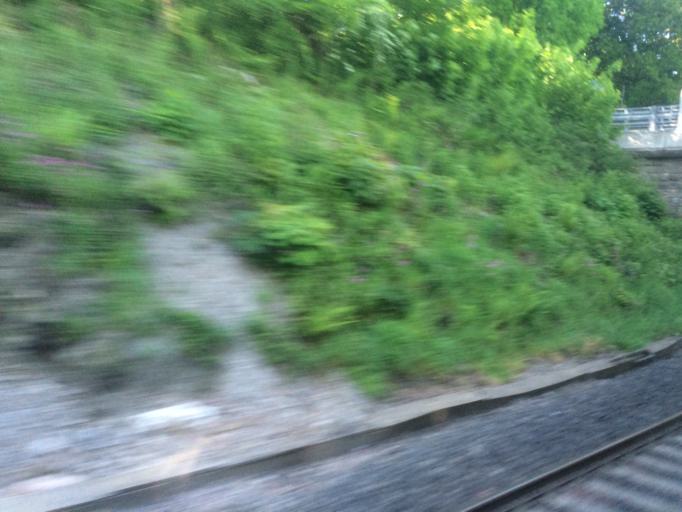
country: GB
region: Scotland
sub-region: North Lanarkshire
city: Cumbernauld
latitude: 55.9753
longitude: -3.9447
